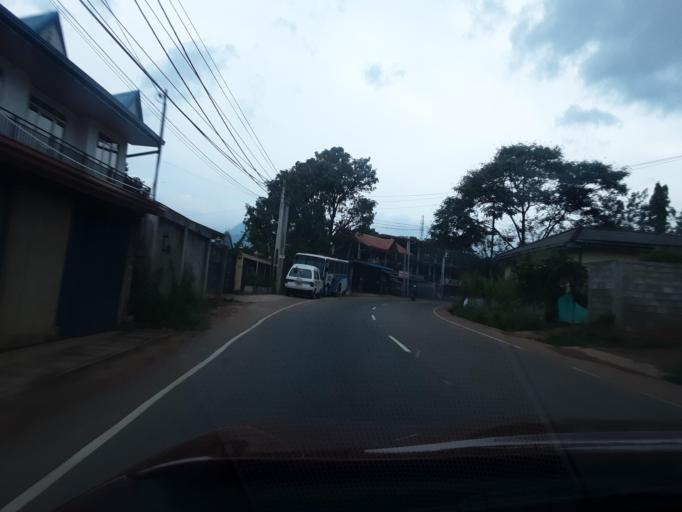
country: LK
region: Central
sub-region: Nuwara Eliya District
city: Nuwara Eliya
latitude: 6.9016
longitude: 80.8985
